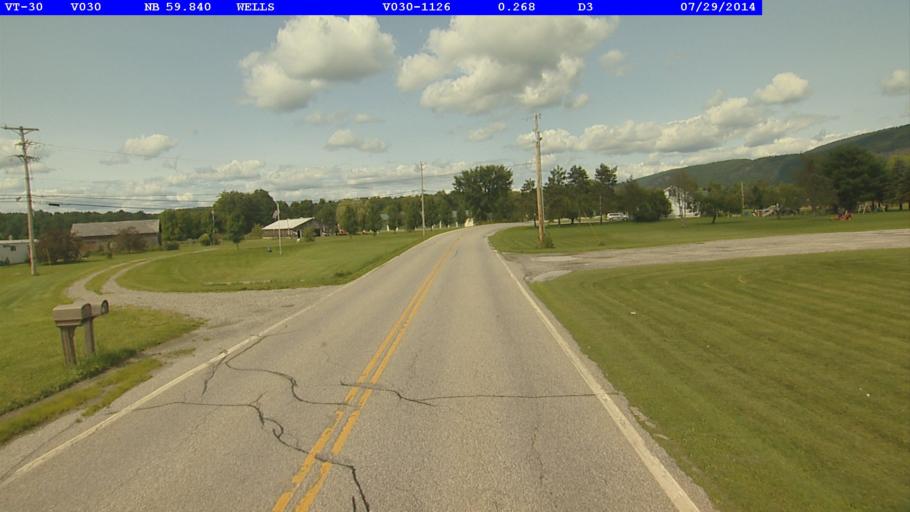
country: US
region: New York
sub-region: Washington County
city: Granville
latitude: 43.4116
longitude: -73.2252
